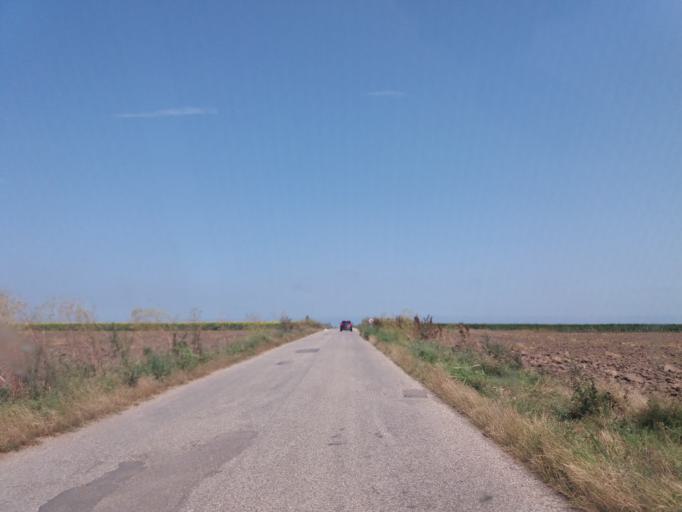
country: RO
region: Constanta
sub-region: Comuna Corbu
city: Corbu
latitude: 44.4238
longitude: 28.6837
